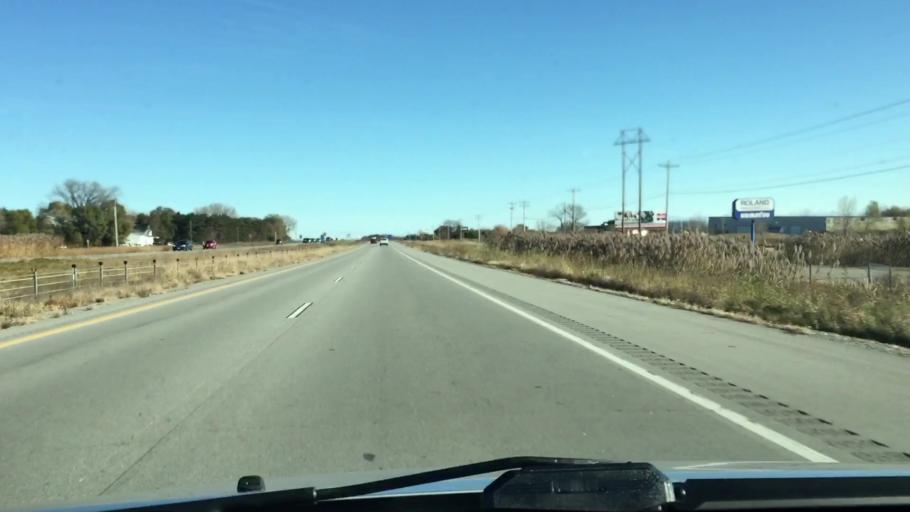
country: US
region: Wisconsin
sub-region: Brown County
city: Wrightstown
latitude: 44.3743
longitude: -88.1708
